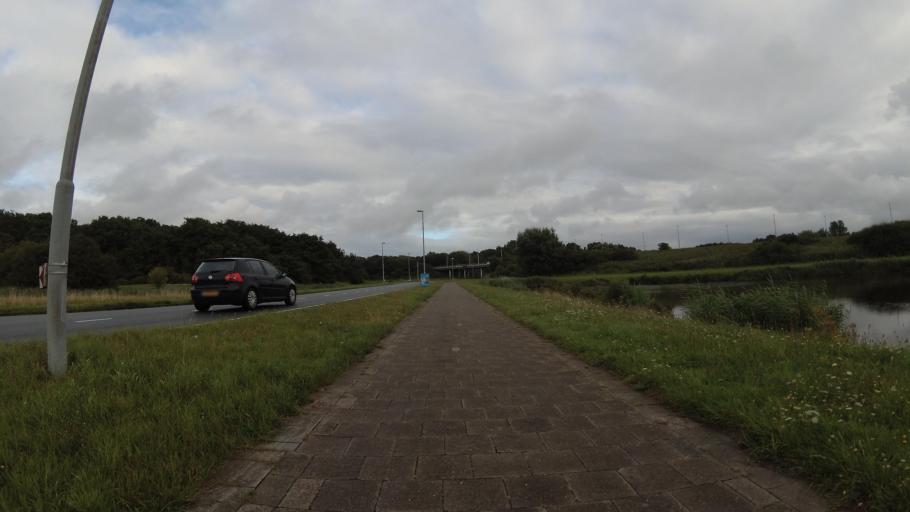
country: NL
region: North Holland
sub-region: Gemeente Den Helder
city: Den Helder
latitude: 52.9419
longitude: 4.7582
